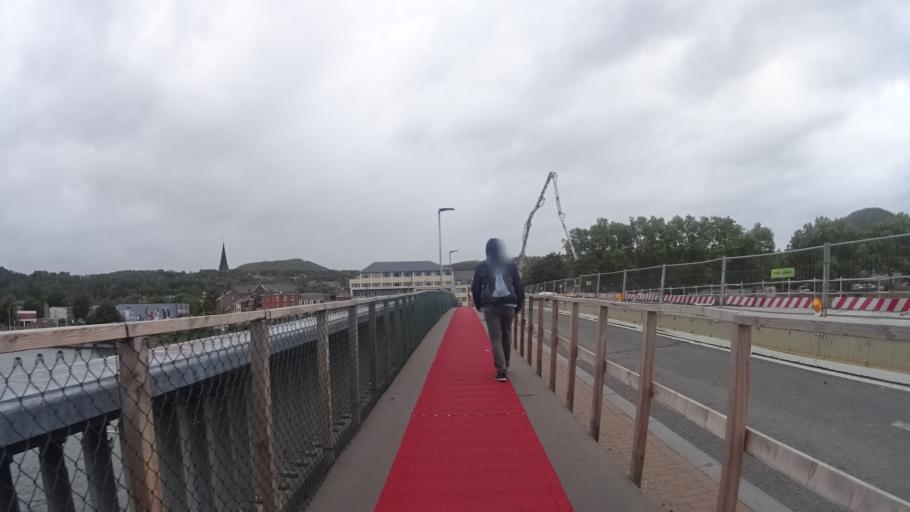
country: BE
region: Wallonia
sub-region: Province de Liege
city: Herstal
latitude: 50.6489
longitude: 5.6020
